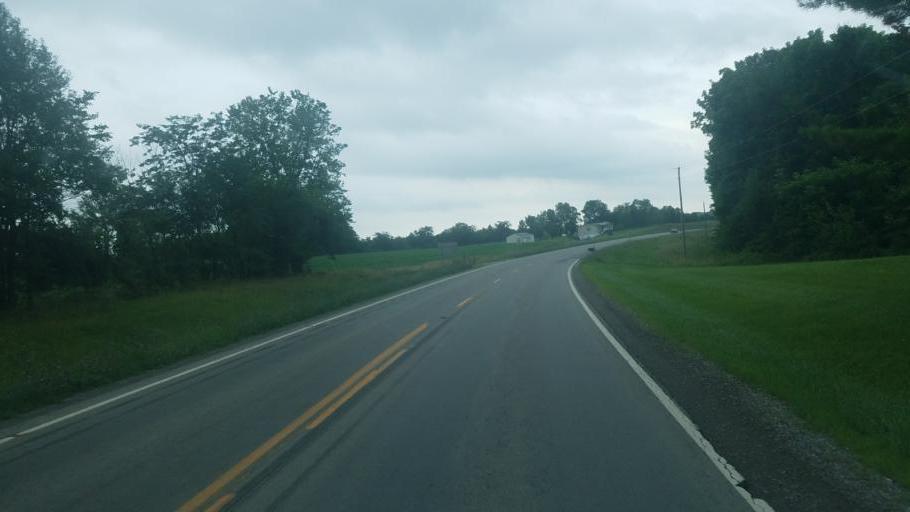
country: US
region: Ohio
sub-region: Logan County
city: Russells Point
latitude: 40.5861
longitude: -83.8404
